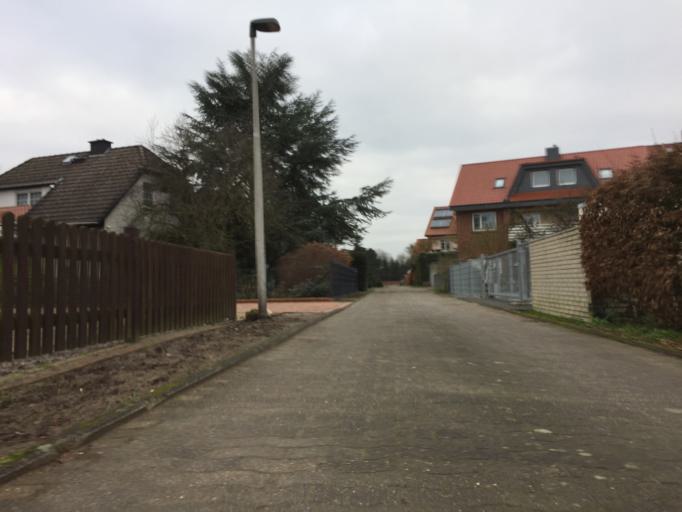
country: DE
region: Lower Saxony
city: Sulingen
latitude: 52.6869
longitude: 8.8059
